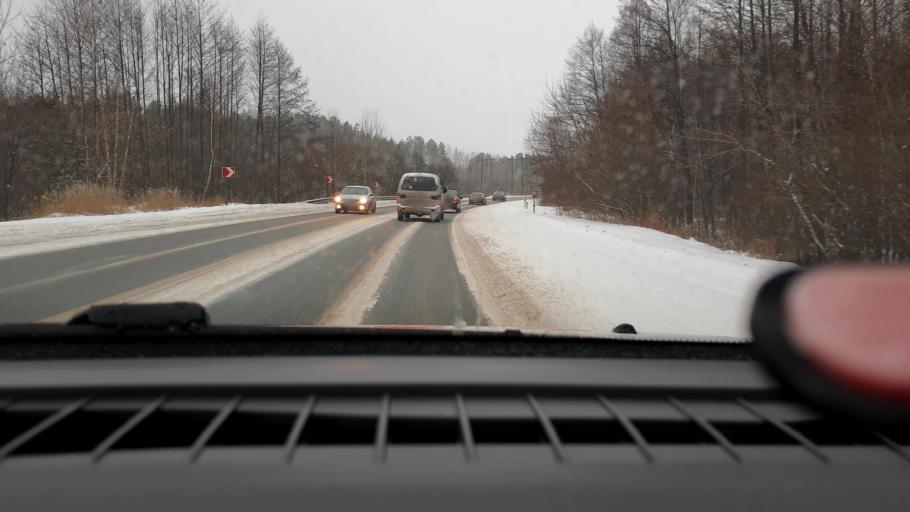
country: RU
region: Nizjnij Novgorod
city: Lukino
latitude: 56.4264
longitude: 43.6267
